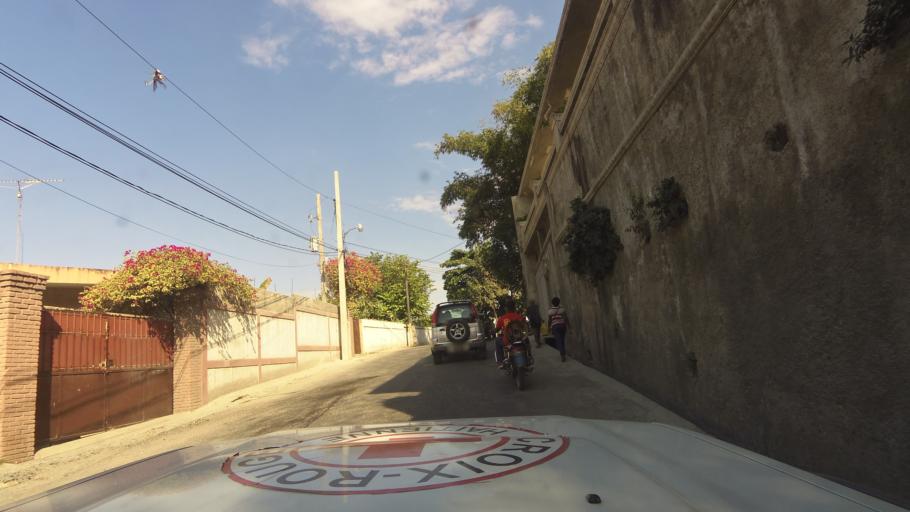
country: HT
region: Ouest
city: Petionville
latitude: 18.5321
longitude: -72.2868
